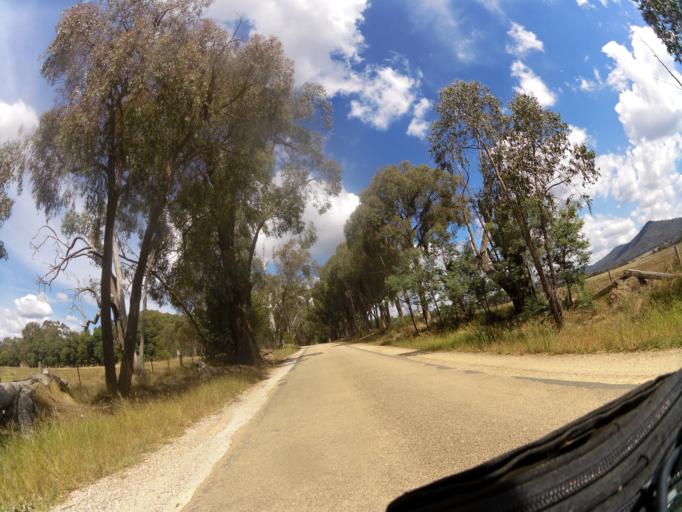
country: AU
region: Victoria
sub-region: Benalla
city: Benalla
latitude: -36.7733
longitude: 145.9745
